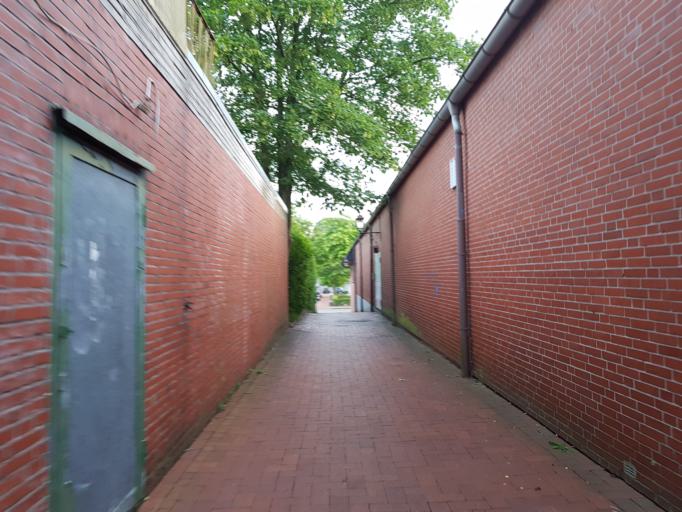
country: DE
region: Lower Saxony
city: Wittmund
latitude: 53.5754
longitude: 7.7819
